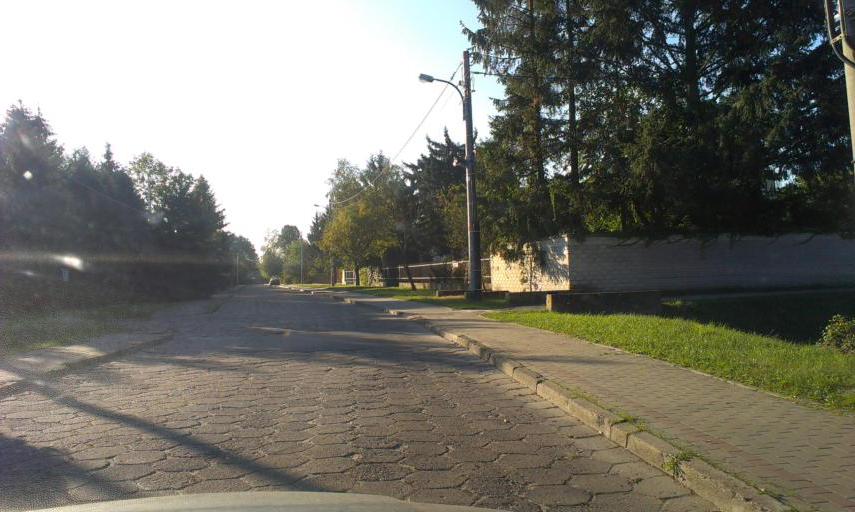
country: PL
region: Masovian Voivodeship
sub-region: Warszawa
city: Kabaty
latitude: 52.1189
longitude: 21.0965
